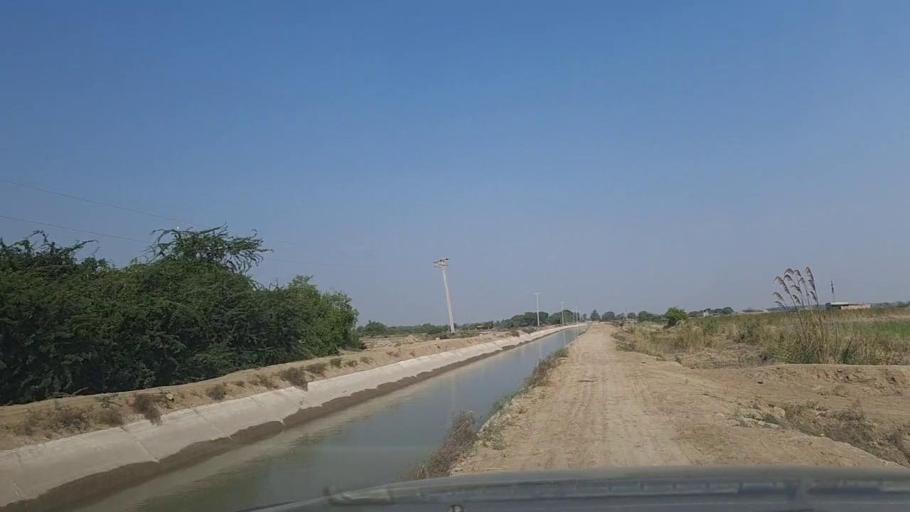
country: PK
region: Sindh
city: Mirpur Sakro
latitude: 24.5254
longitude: 67.8109
